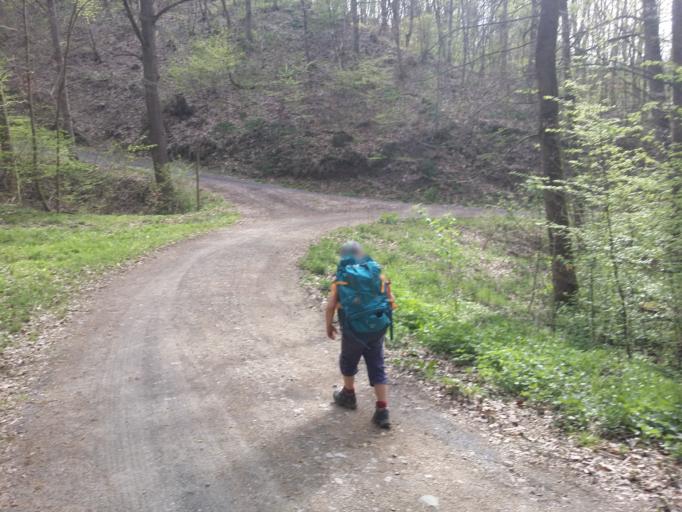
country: DE
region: Saxony-Anhalt
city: Harzgerode
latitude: 51.6650
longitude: 11.1633
